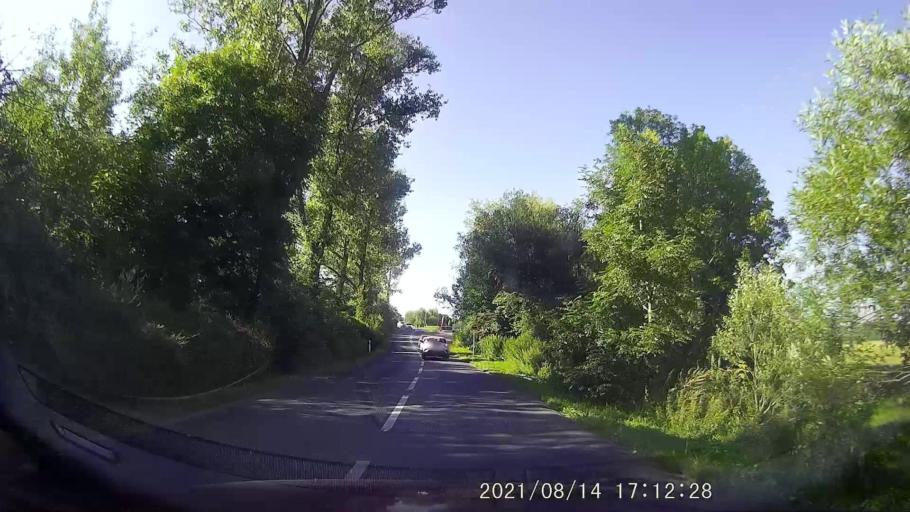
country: PL
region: Lower Silesian Voivodeship
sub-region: Powiat jeleniogorski
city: Myslakowice
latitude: 50.8436
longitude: 15.7867
